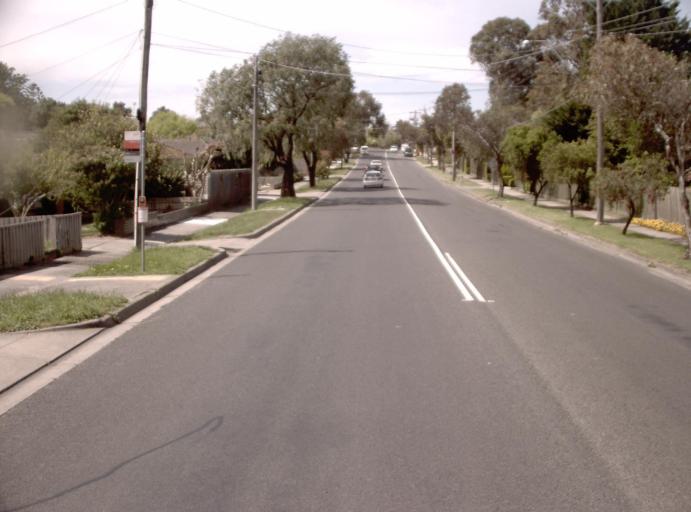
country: AU
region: Victoria
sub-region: Maroondah
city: Croydon North
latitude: -37.7938
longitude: 145.3017
